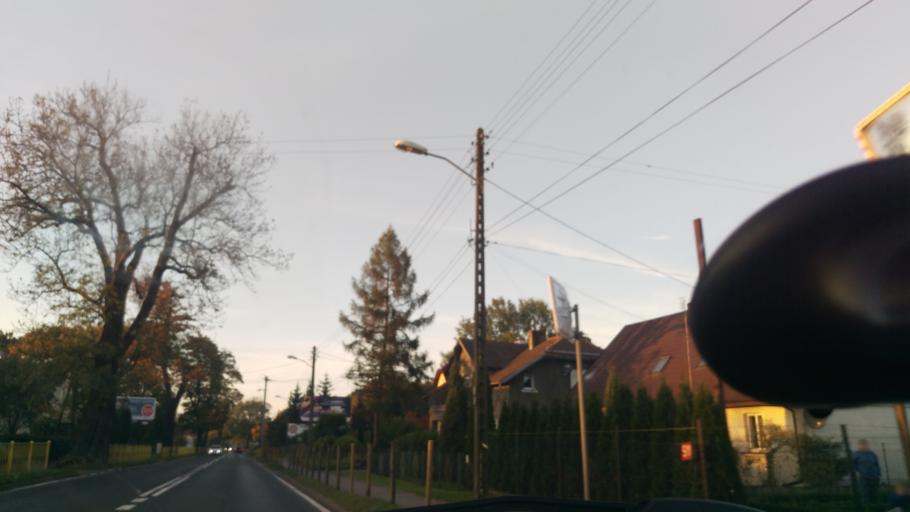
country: PL
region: West Pomeranian Voivodeship
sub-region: Powiat gryfinski
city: Stare Czarnowo
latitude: 53.3476
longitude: 14.7489
